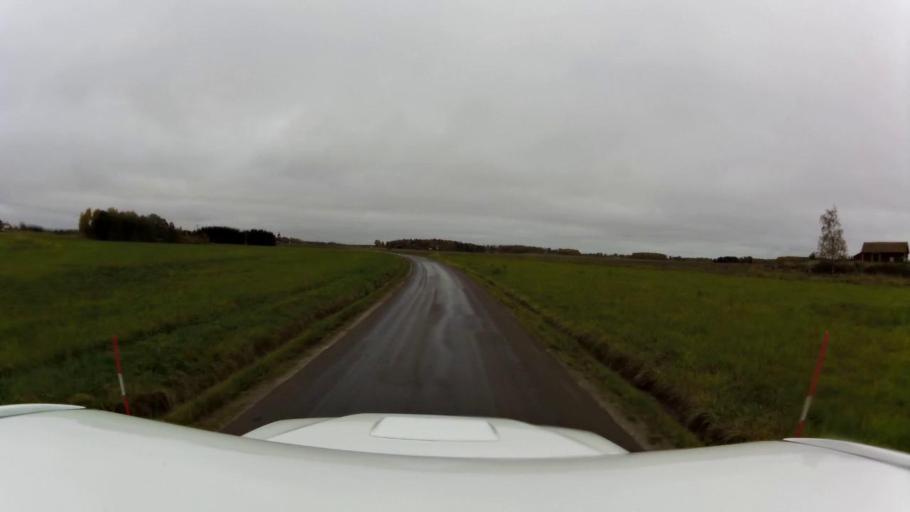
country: SE
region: OEstergoetland
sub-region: Linkopings Kommun
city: Ekangen
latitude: 58.4616
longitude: 15.7030
